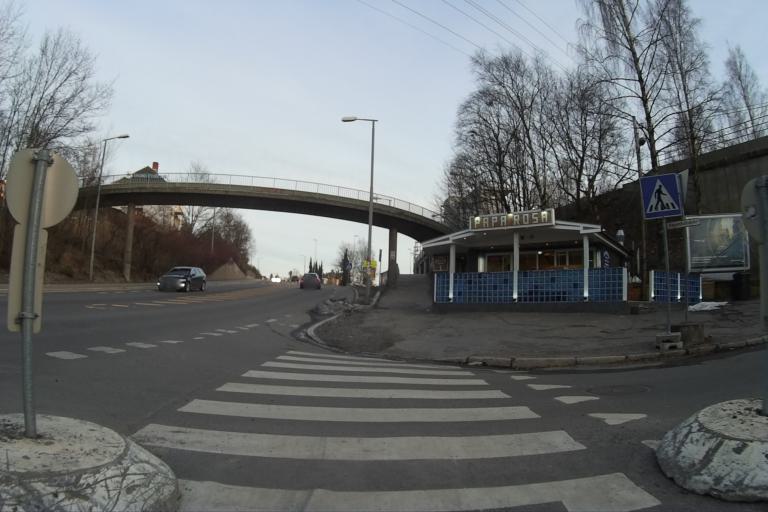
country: NO
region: Oslo
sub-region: Oslo
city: Oslo
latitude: 59.9069
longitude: 10.8192
